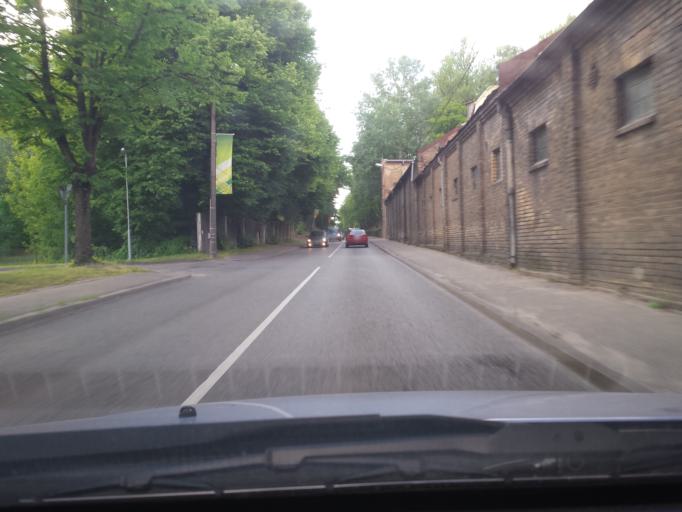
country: LV
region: Riga
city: Riga
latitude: 56.9592
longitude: 24.0691
